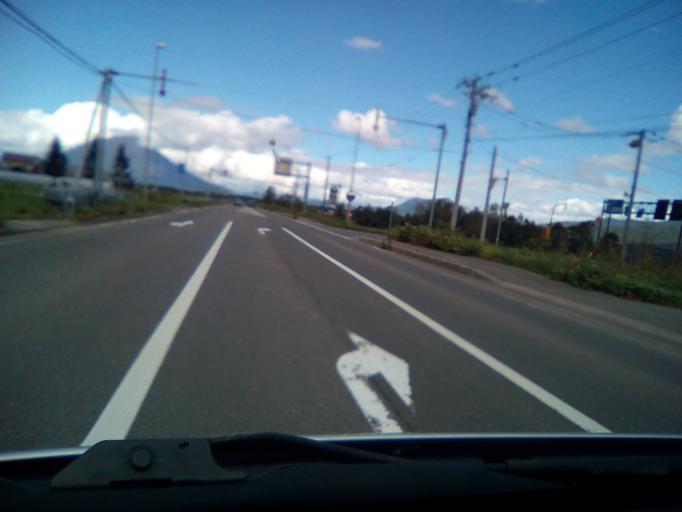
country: JP
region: Hokkaido
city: Date
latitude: 42.6424
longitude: 140.8034
